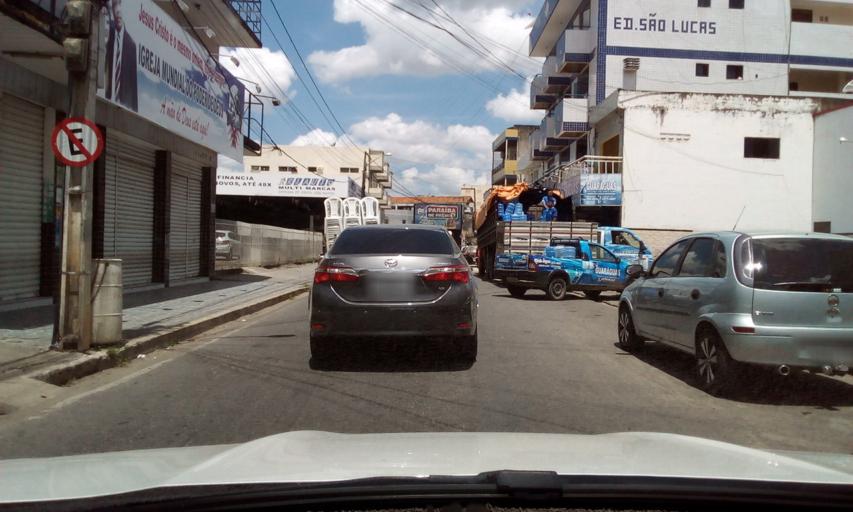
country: BR
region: Paraiba
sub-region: Guarabira
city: Guarabira
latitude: -6.8534
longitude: -35.4935
